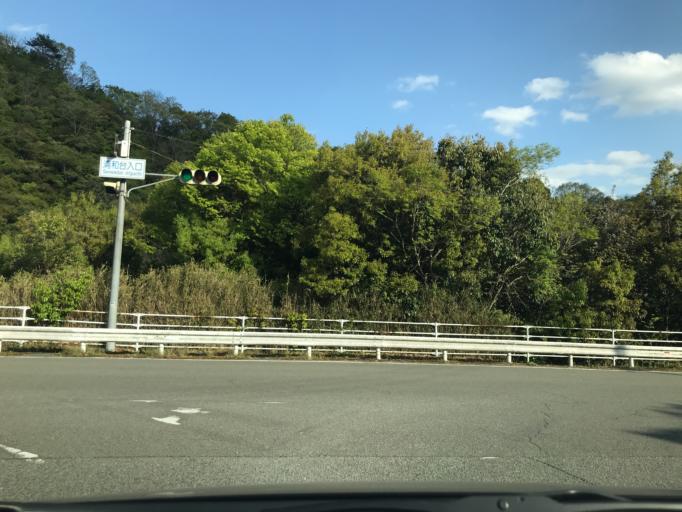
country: JP
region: Hyogo
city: Kawanishi
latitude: 34.8694
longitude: 135.3968
